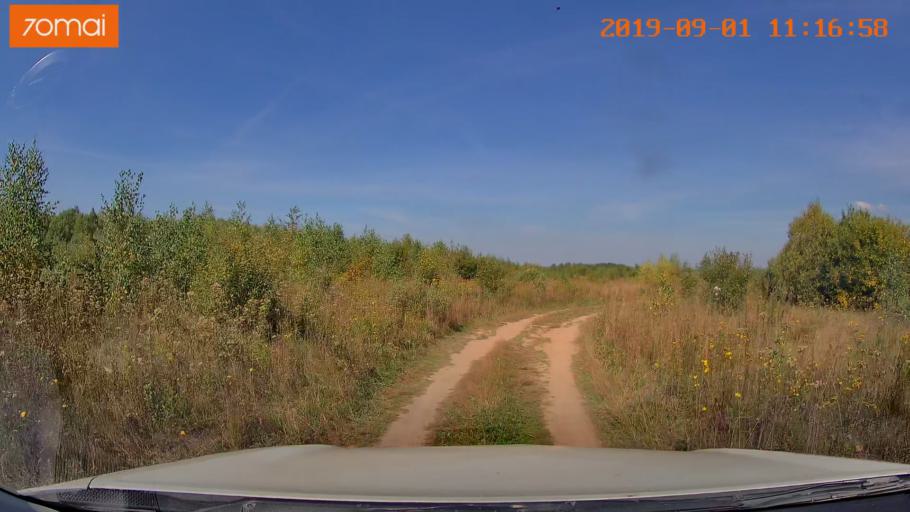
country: RU
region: Kaluga
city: Detchino
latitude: 54.8243
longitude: 36.3675
